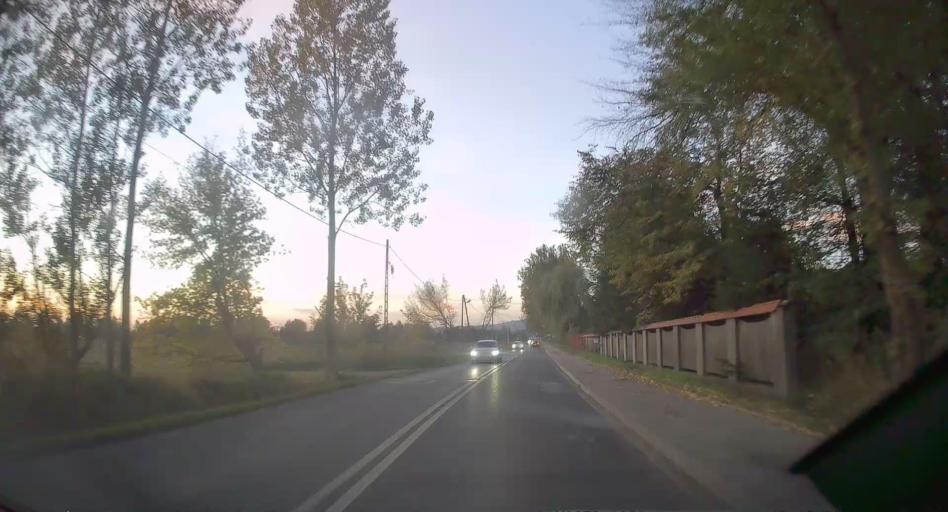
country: PL
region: Lesser Poland Voivodeship
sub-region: Powiat krakowski
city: Zabierzow
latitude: 50.1187
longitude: 19.8262
